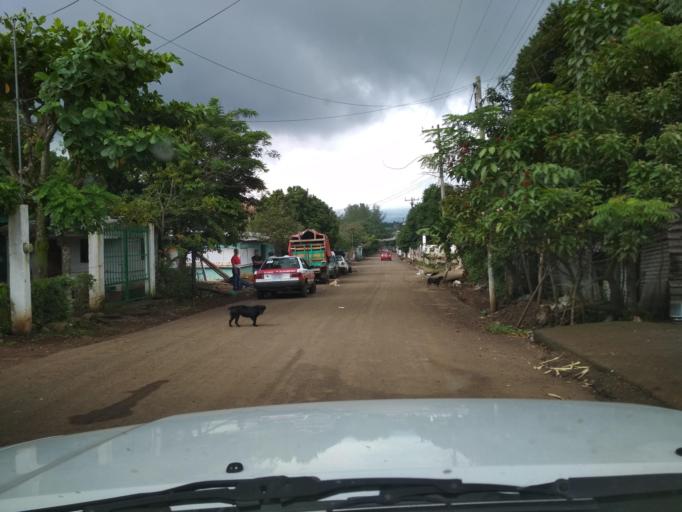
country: MX
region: Veracruz
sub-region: San Andres Tuxtla
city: El Huidero
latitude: 18.3871
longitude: -95.1789
